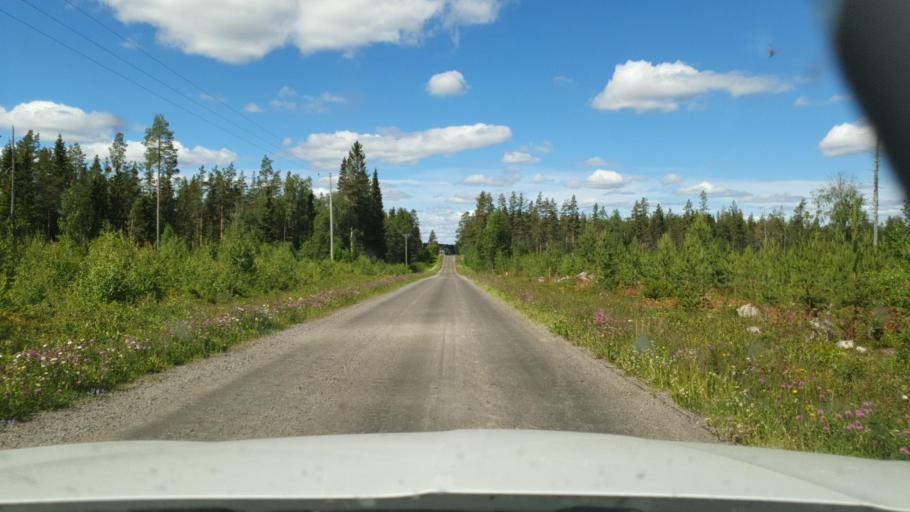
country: SE
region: Vaesterbotten
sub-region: Skelleftea Kommun
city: Backa
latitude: 65.1788
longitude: 21.0791
